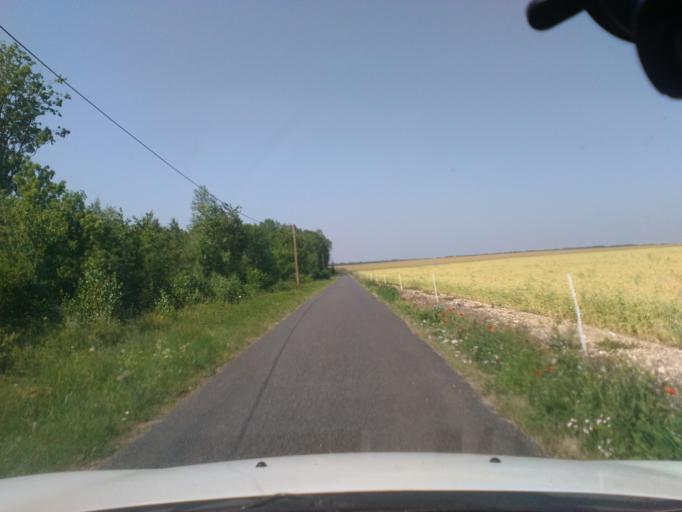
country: FR
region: Lorraine
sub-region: Departement des Vosges
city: Liffol-le-Grand
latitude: 48.3108
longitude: 5.4195
